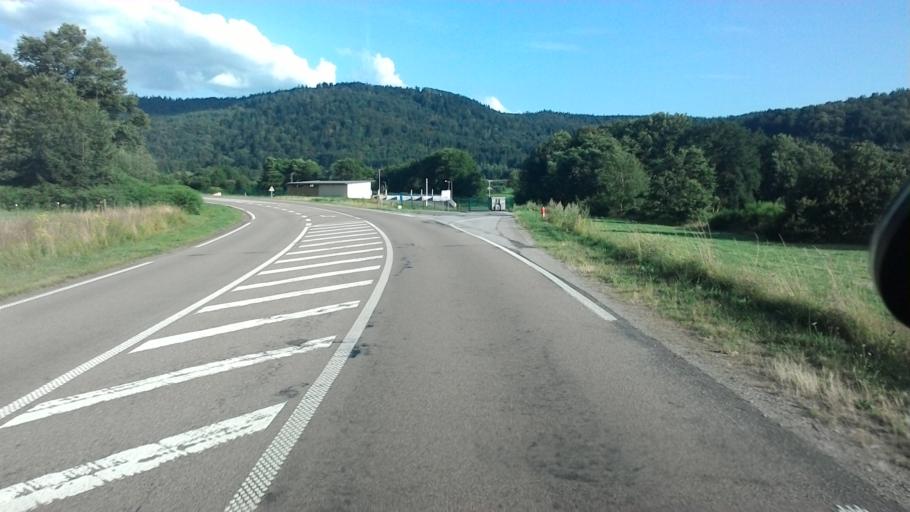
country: FR
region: Lorraine
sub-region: Departement des Vosges
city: Rupt-sur-Moselle
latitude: 47.9132
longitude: 6.6688
